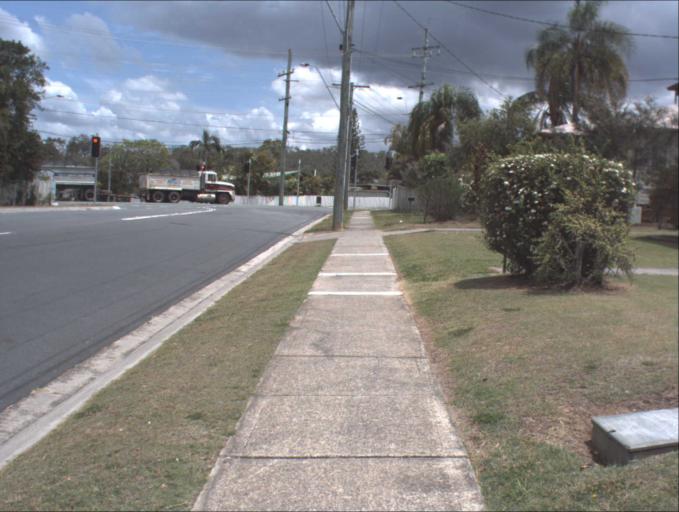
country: AU
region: Queensland
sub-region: Logan
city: Beenleigh
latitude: -27.7227
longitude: 153.2063
